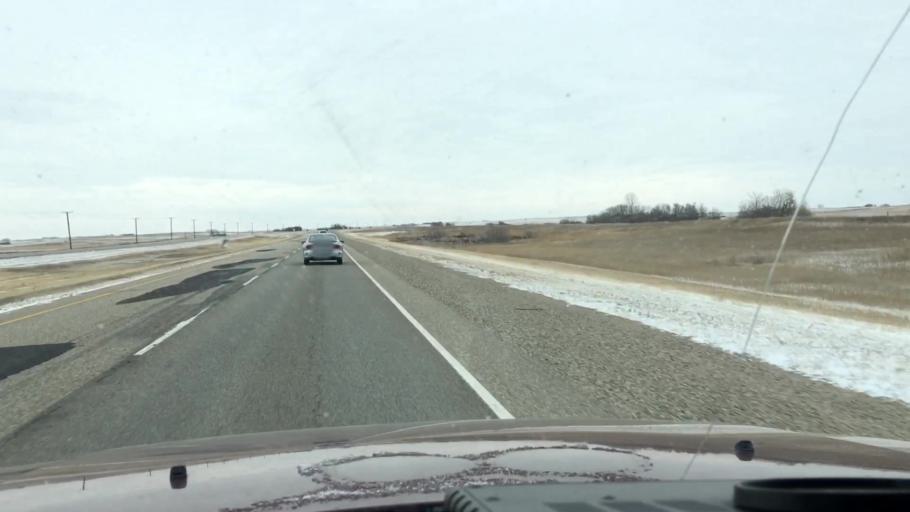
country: CA
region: Saskatchewan
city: Watrous
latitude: 51.4422
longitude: -106.2109
